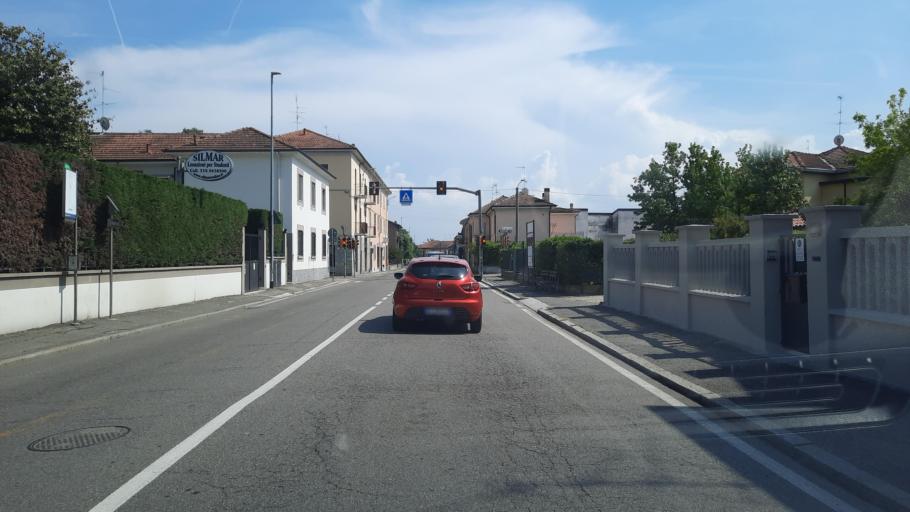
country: IT
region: Lombardy
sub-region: Provincia di Pavia
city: Pavia
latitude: 45.1910
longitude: 9.1323
